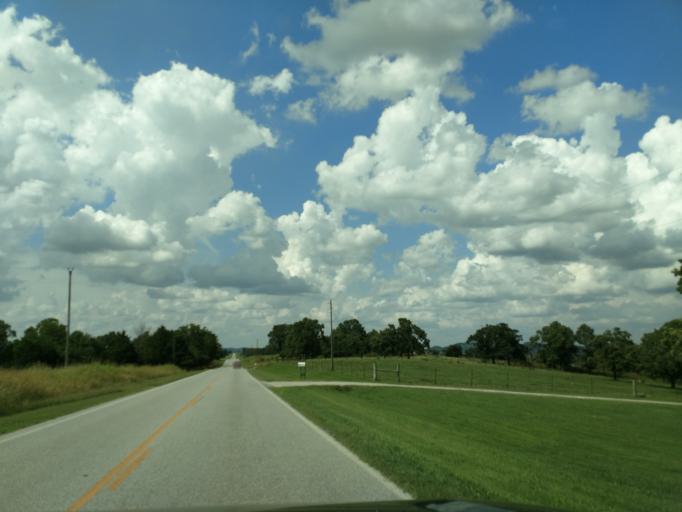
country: US
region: Arkansas
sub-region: Carroll County
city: Berryville
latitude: 36.4389
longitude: -93.5562
